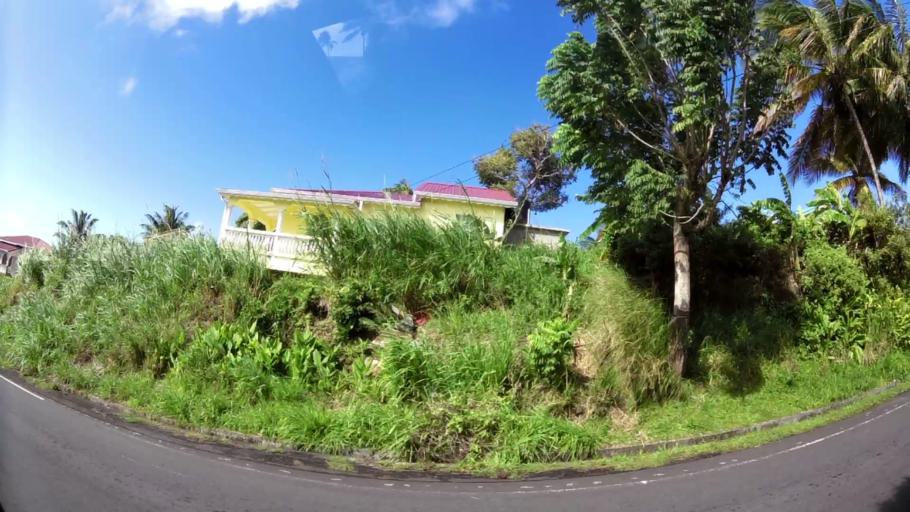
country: LC
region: Choiseul Quarter
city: Choiseul
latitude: 13.8045
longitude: -61.0362
